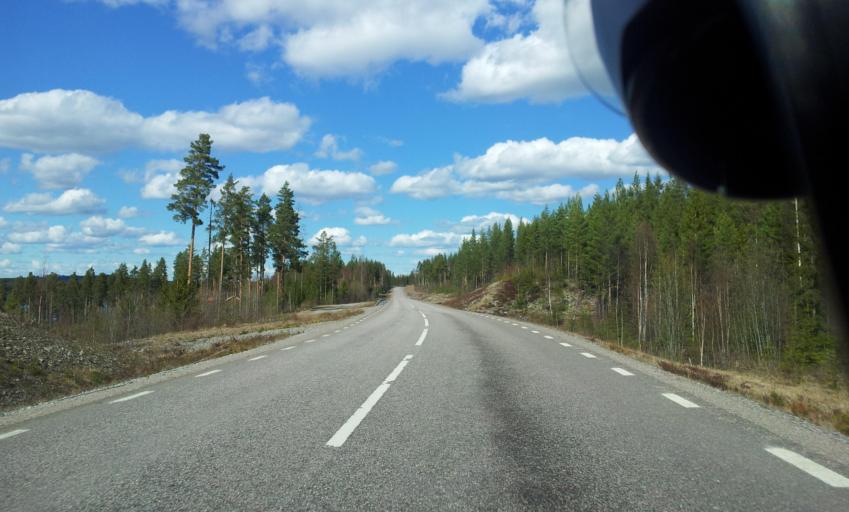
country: SE
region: Gaevleborg
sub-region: Ovanakers Kommun
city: Edsbyn
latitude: 61.2171
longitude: 15.8773
